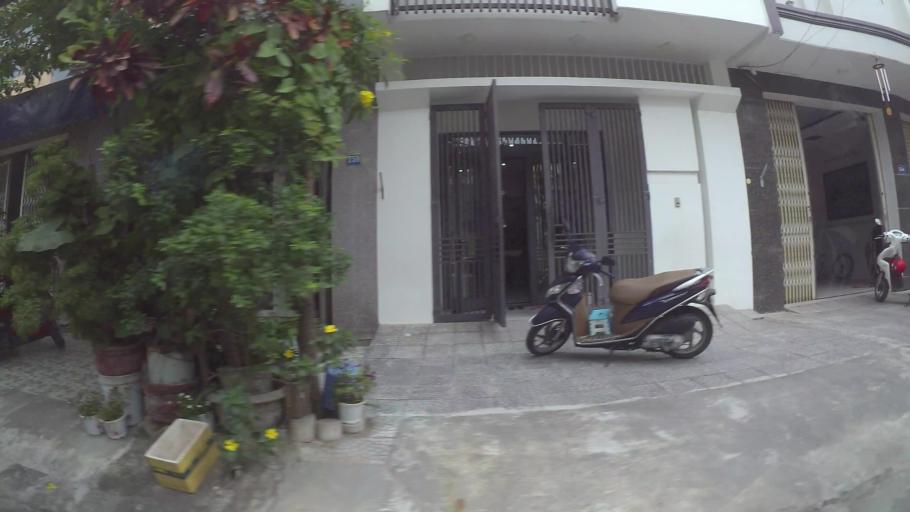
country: VN
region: Da Nang
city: Lien Chieu
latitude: 16.0782
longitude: 108.1710
